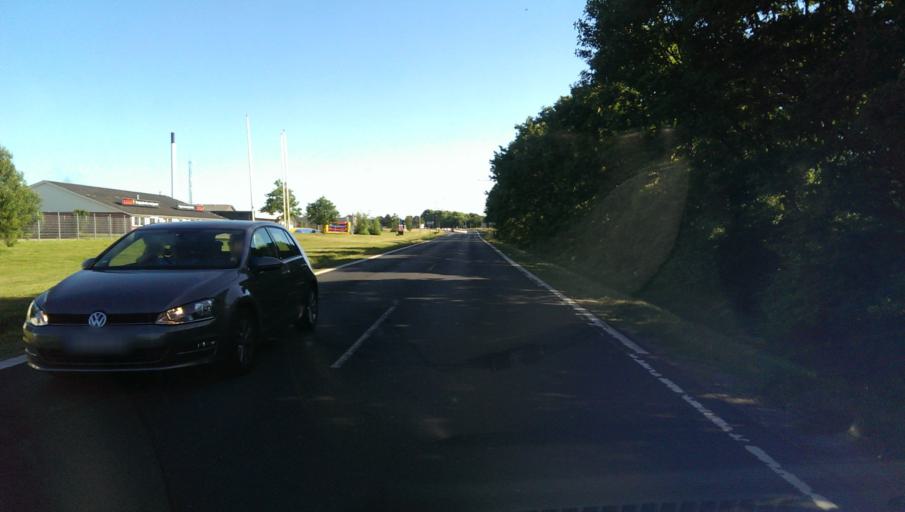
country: DK
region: South Denmark
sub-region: Esbjerg Kommune
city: Esbjerg
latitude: 55.5073
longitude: 8.4055
